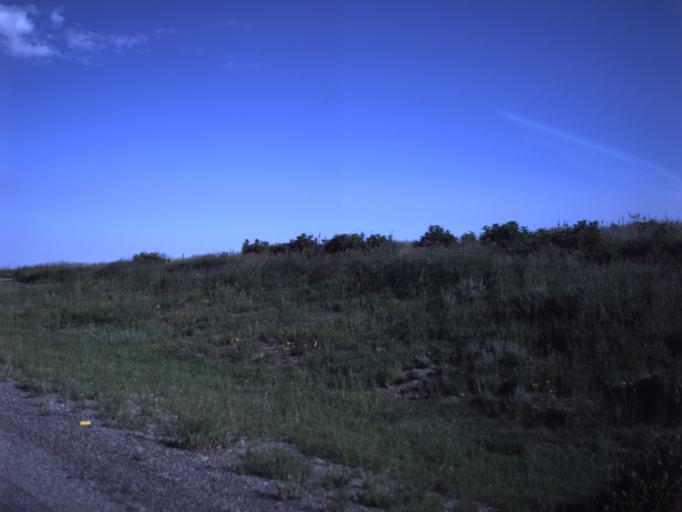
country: US
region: Utah
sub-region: Sanpete County
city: Fairview
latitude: 39.6196
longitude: -111.2868
